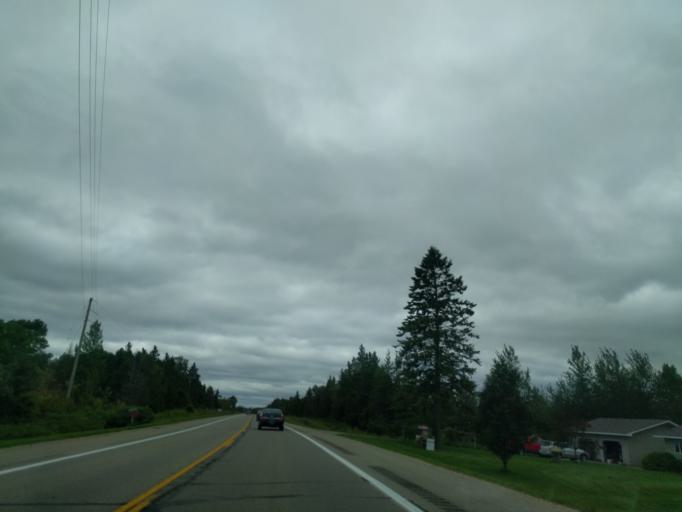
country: US
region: Michigan
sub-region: Delta County
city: Escanaba
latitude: 45.6393
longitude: -87.1973
